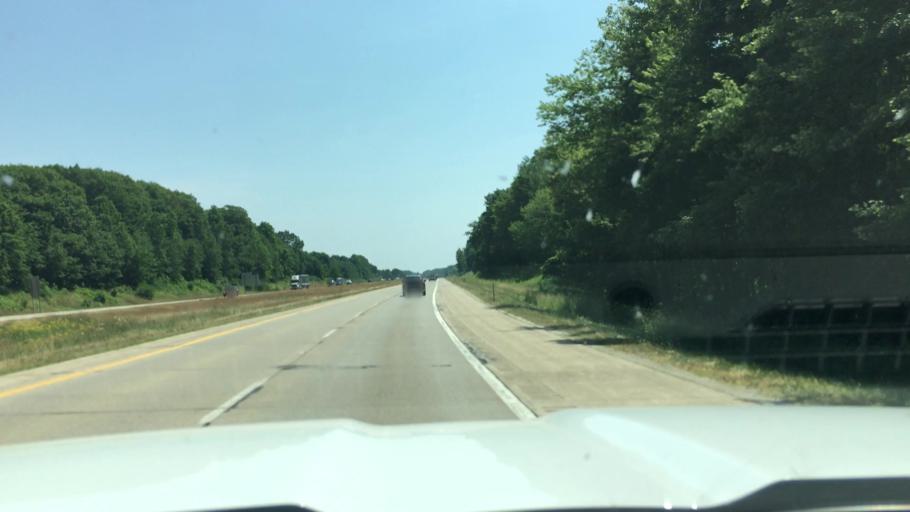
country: US
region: Michigan
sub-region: Clinton County
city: DeWitt
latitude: 42.8072
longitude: -84.6220
